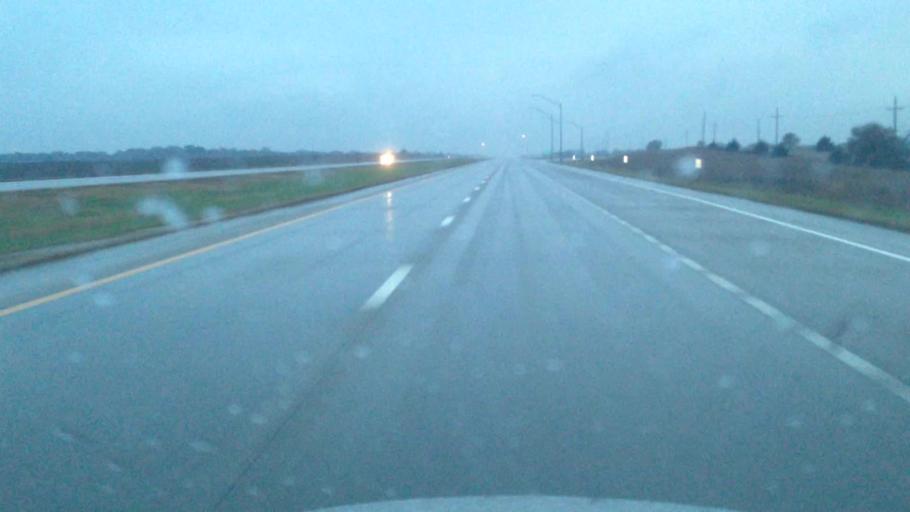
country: US
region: Kansas
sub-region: Douglas County
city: Baldwin City
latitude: 38.7247
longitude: -95.2686
